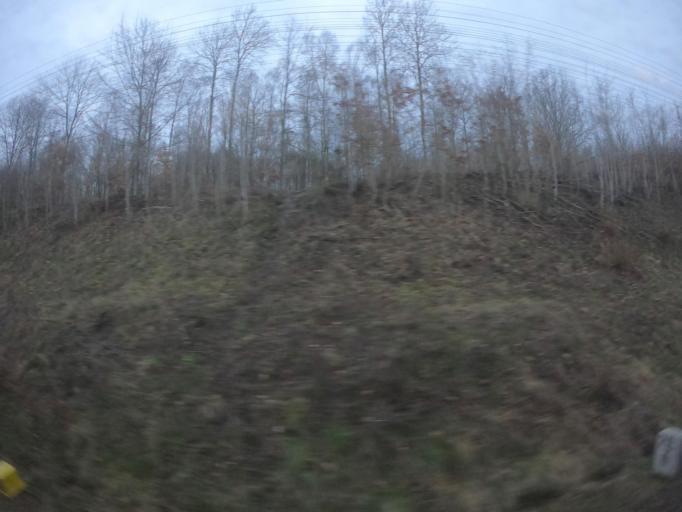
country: PL
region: West Pomeranian Voivodeship
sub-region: Powiat szczecinecki
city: Borne Sulinowo
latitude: 53.6408
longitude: 16.5058
